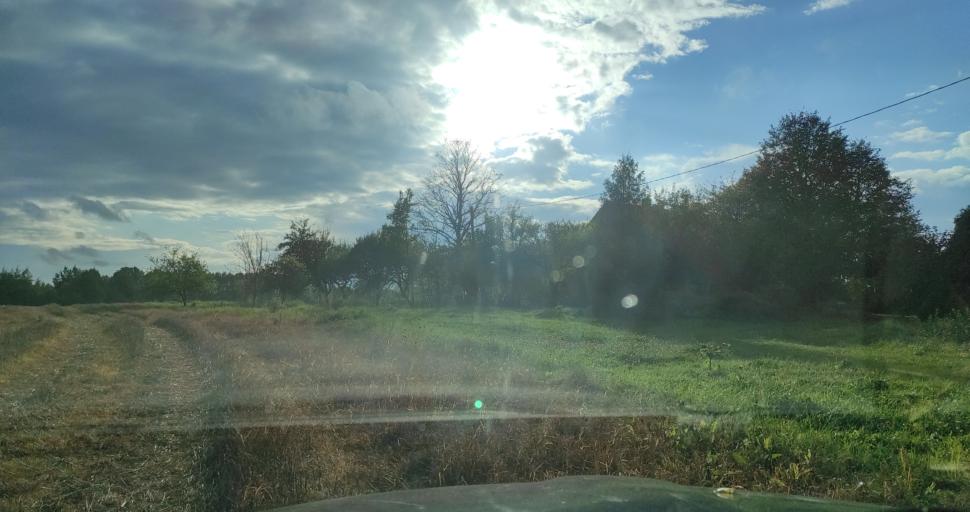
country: LV
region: Talsu Rajons
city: Sabile
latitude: 56.9003
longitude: 22.4205
